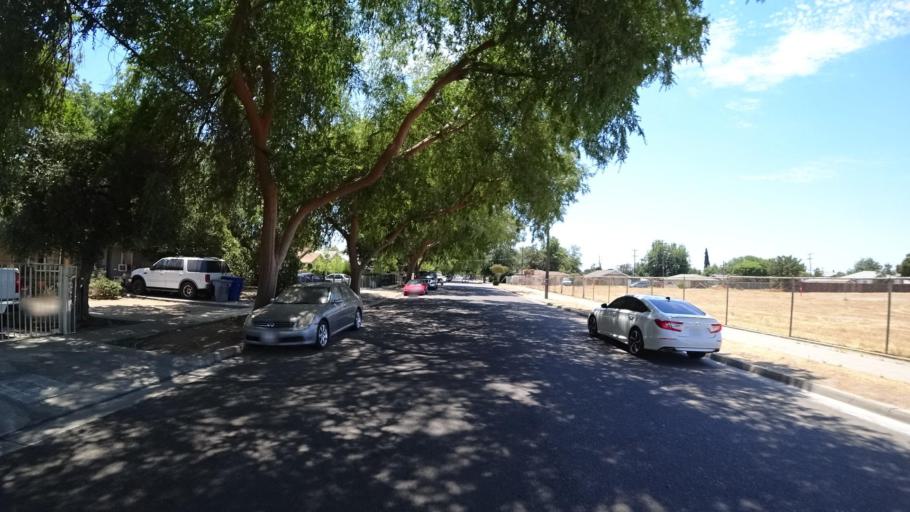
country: US
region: California
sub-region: Fresno County
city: Fresno
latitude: 36.7351
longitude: -119.7612
